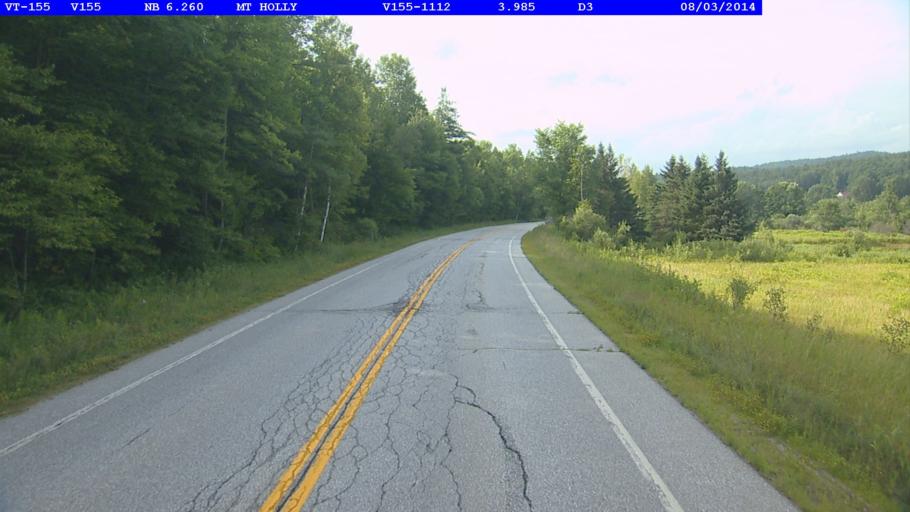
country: US
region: Vermont
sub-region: Rutland County
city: Rutland
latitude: 43.4052
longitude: -72.8376
